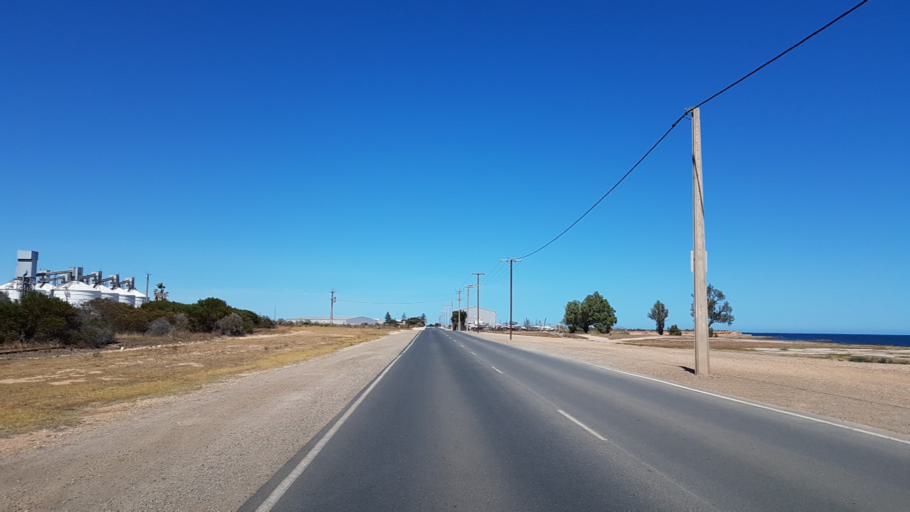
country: AU
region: South Australia
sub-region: Copper Coast
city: Wallaroo
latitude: -33.9312
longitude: 137.6135
